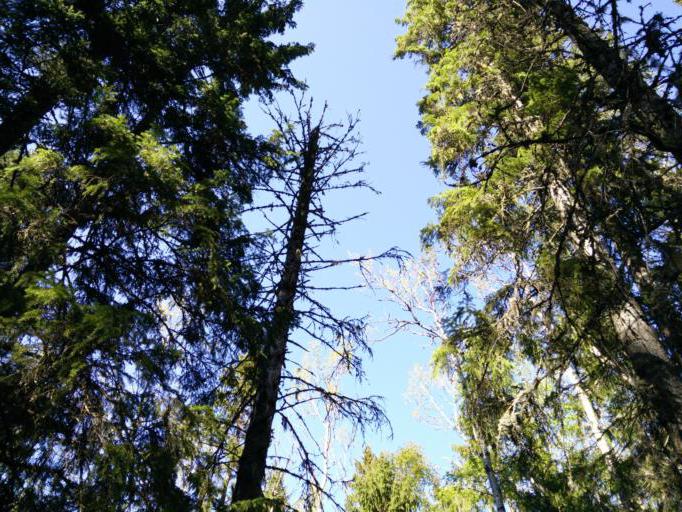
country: SE
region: Vaesternorrland
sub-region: OErnskoeldsviks Kommun
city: Kopmanholmen
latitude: 63.1205
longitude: 18.5148
